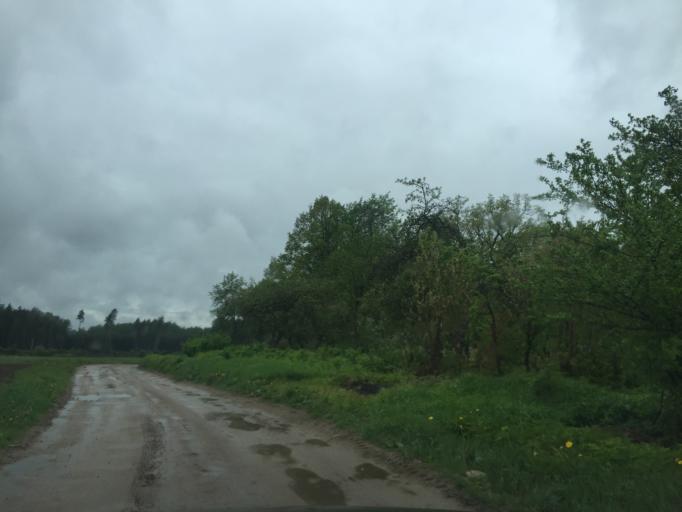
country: LV
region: Ogre
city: Jumprava
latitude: 56.6631
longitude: 25.0059
